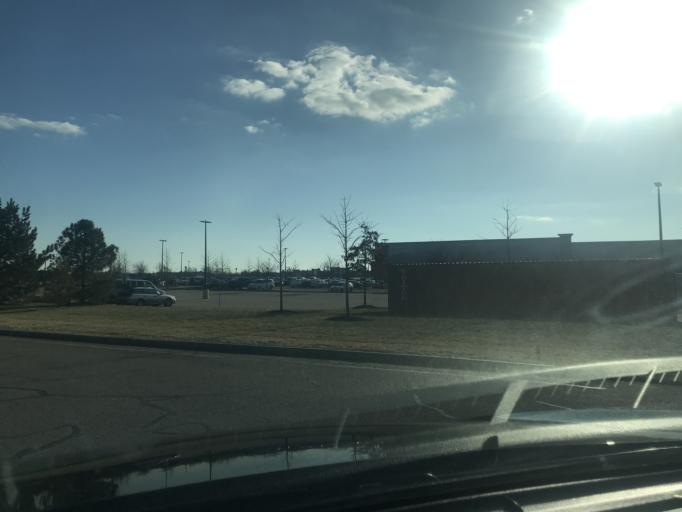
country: US
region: Massachusetts
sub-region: Plymouth County
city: North Plymouth
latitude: 41.9570
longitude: -70.7169
